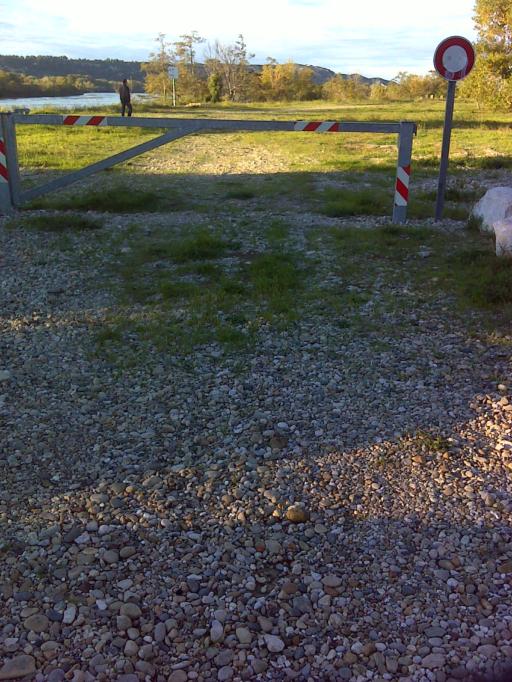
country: FR
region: Provence-Alpes-Cote d'Azur
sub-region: Departement du Vaucluse
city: Avignon
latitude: 43.9654
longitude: 4.8167
